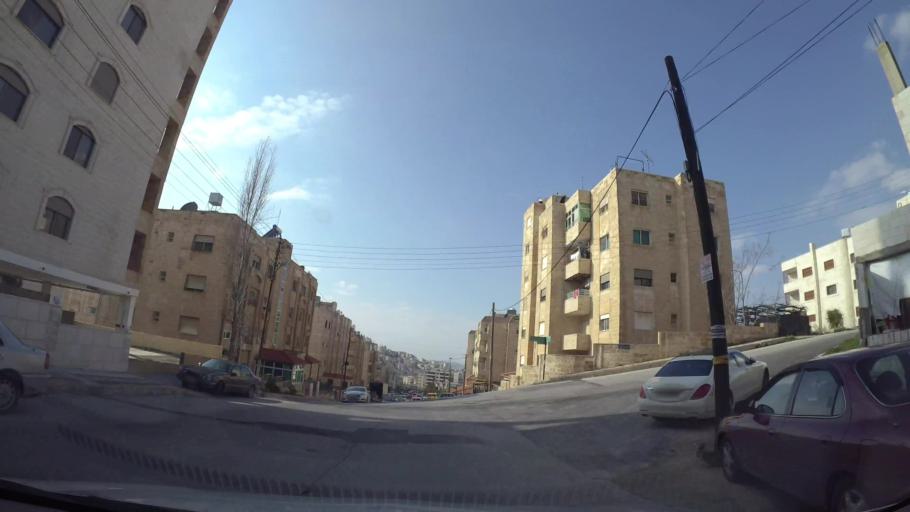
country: JO
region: Amman
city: Al Jubayhah
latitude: 32.0203
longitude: 35.8482
